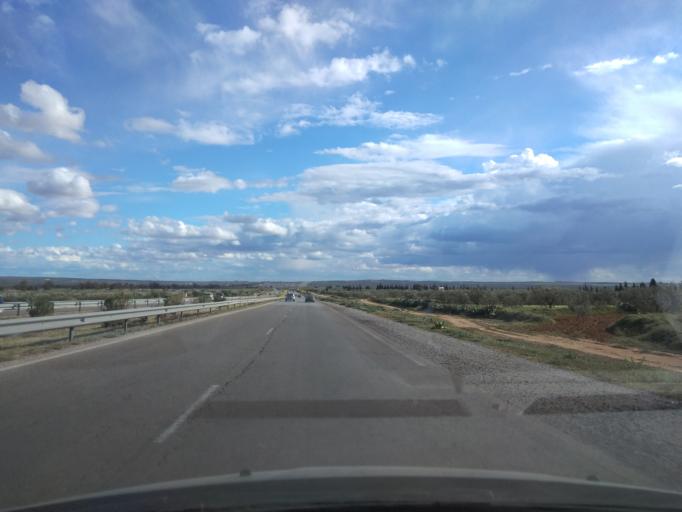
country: TN
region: Al Munastir
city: Manzil Kamil
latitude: 35.6026
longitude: 10.5998
